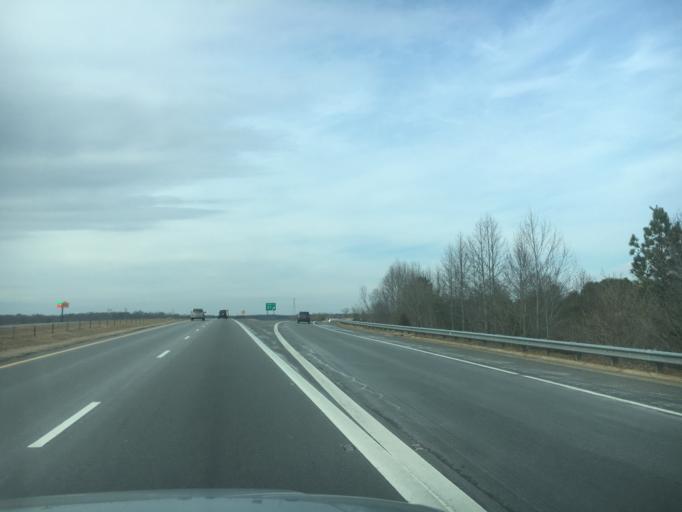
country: US
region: North Carolina
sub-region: Catawba County
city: Newton
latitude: 35.6328
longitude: -81.2952
